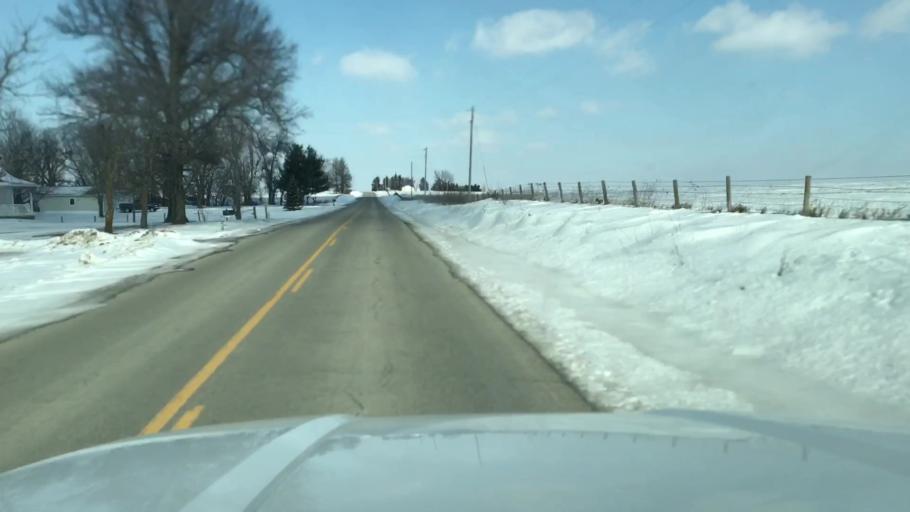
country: US
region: Missouri
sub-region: Nodaway County
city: Maryville
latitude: 40.3679
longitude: -94.7217
